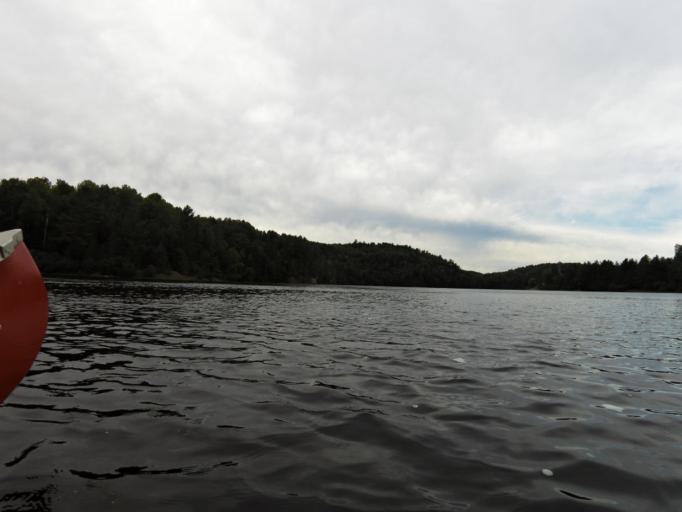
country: CA
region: Quebec
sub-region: Outaouais
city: Wakefield
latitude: 45.8058
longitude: -75.9272
